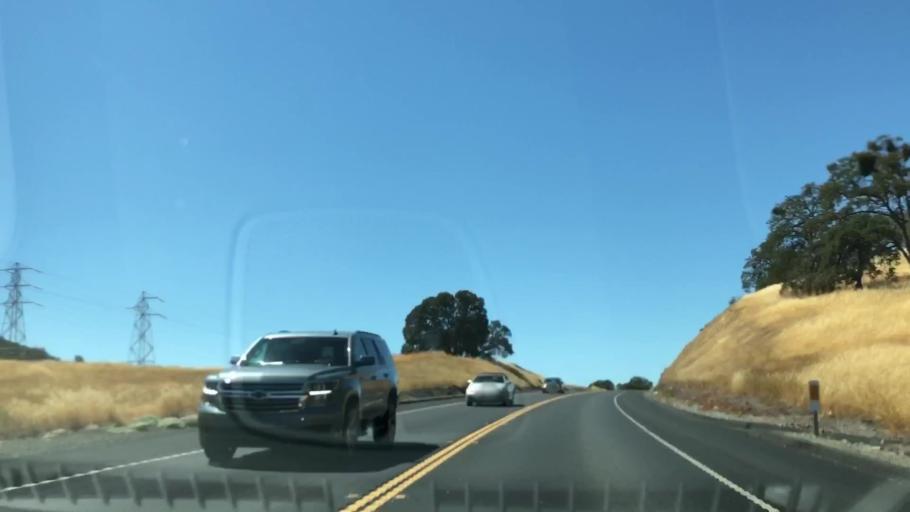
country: US
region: California
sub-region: Calaveras County
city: Copperopolis
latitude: 37.9449
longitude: -120.7002
